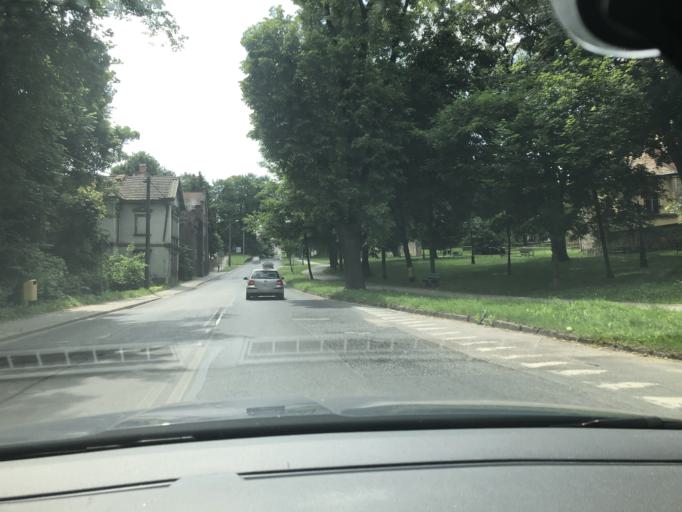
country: PL
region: Lower Silesian Voivodeship
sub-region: Powiat zlotoryjski
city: Zlotoryja
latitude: 51.1247
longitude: 15.9202
